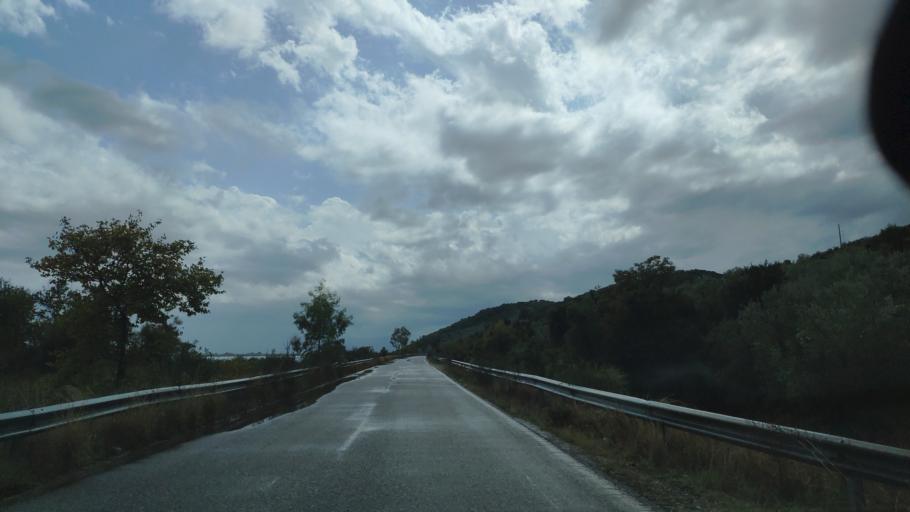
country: GR
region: West Greece
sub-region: Nomos Aitolias kai Akarnanias
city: Lepenou
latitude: 38.6957
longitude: 21.3202
